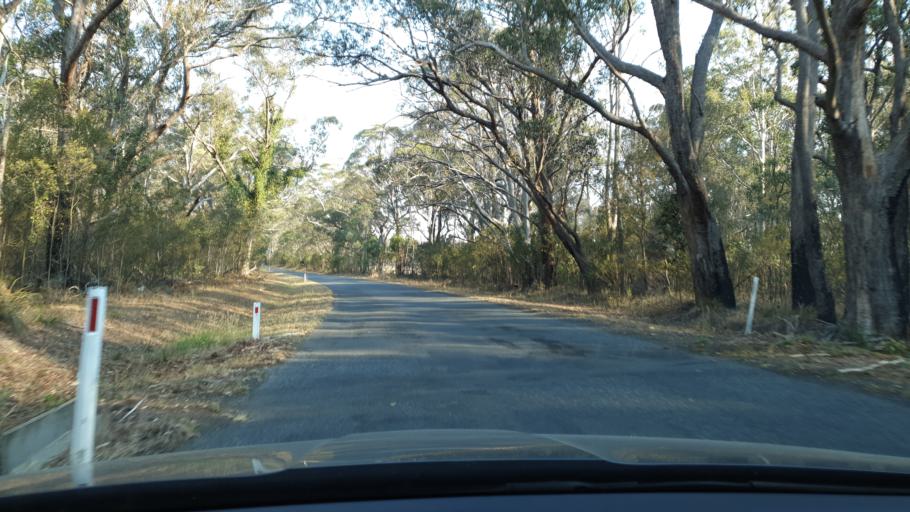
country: AU
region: New South Wales
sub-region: Tenterfield Municipality
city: Carrolls Creek
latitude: -28.6958
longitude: 152.0914
